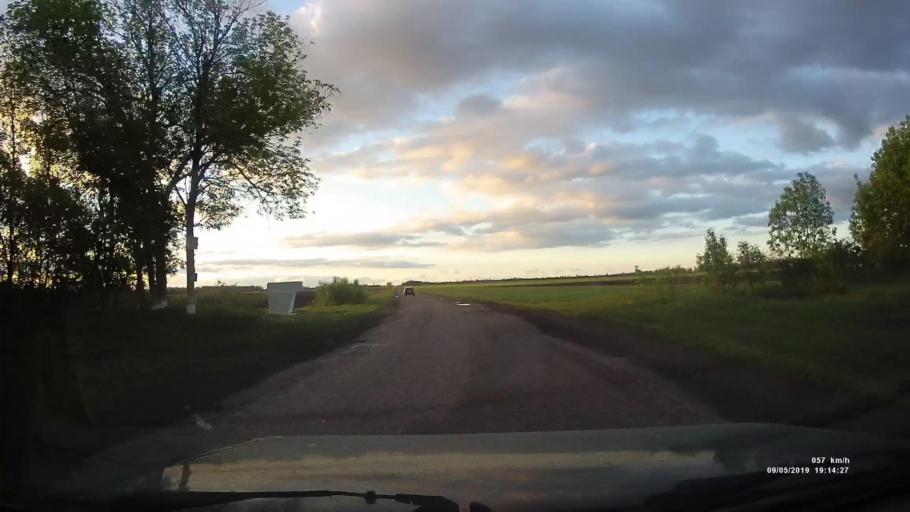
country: RU
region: Krasnodarskiy
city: Kanelovskaya
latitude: 46.7592
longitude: 39.2142
